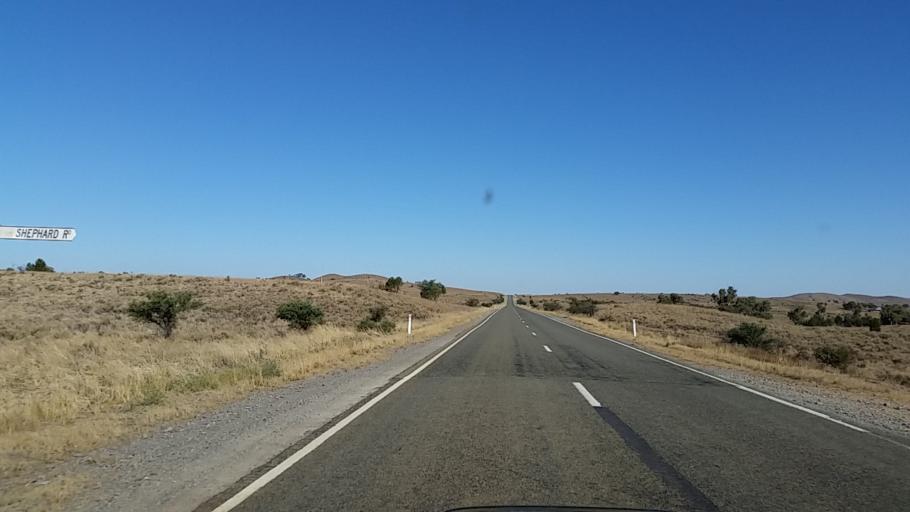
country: AU
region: South Australia
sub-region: Peterborough
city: Peterborough
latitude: -32.5943
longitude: 138.5629
